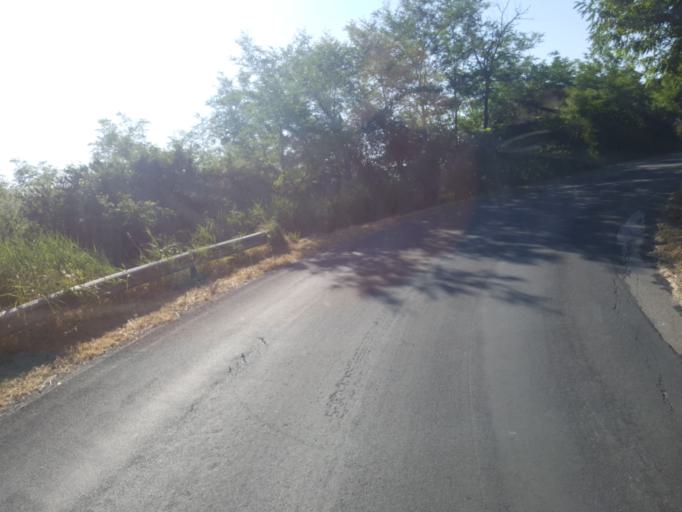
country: IT
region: The Marches
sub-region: Provincia di Pesaro e Urbino
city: Montecalvo in Foglia
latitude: 43.7866
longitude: 12.6242
